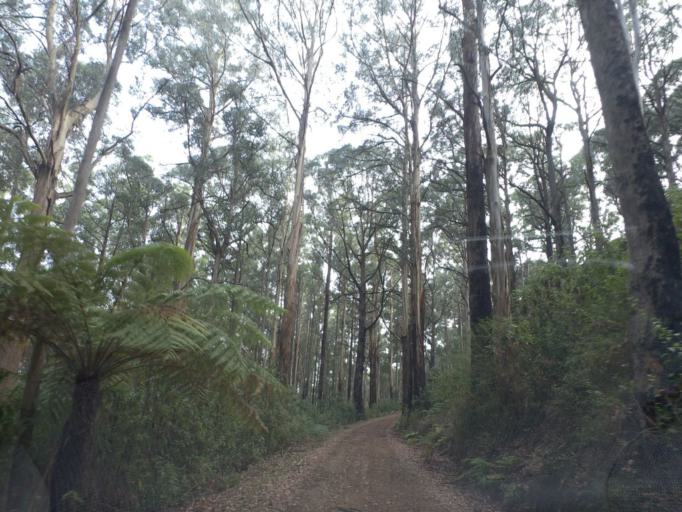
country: AU
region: Victoria
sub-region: Yarra Ranges
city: Healesville
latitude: -37.5816
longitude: 145.5232
